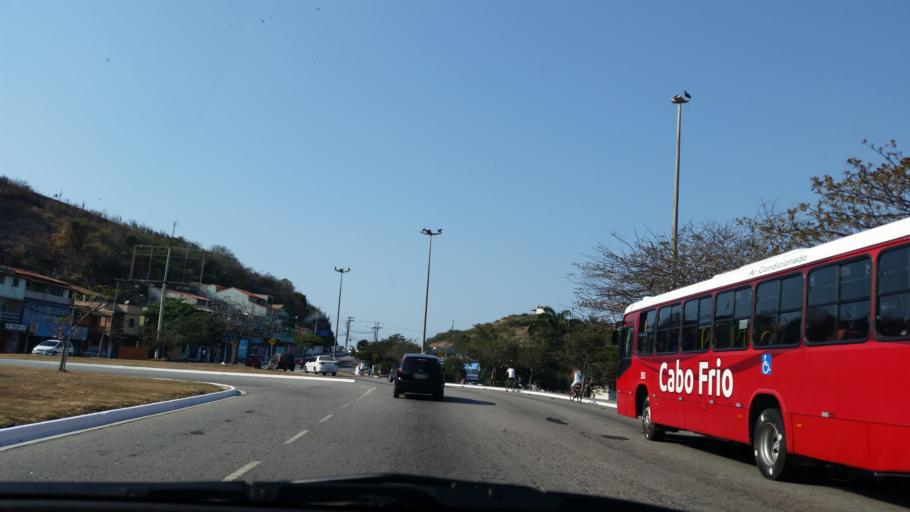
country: BR
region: Rio de Janeiro
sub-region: Cabo Frio
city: Cabo Frio
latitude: -22.8746
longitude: -42.0229
